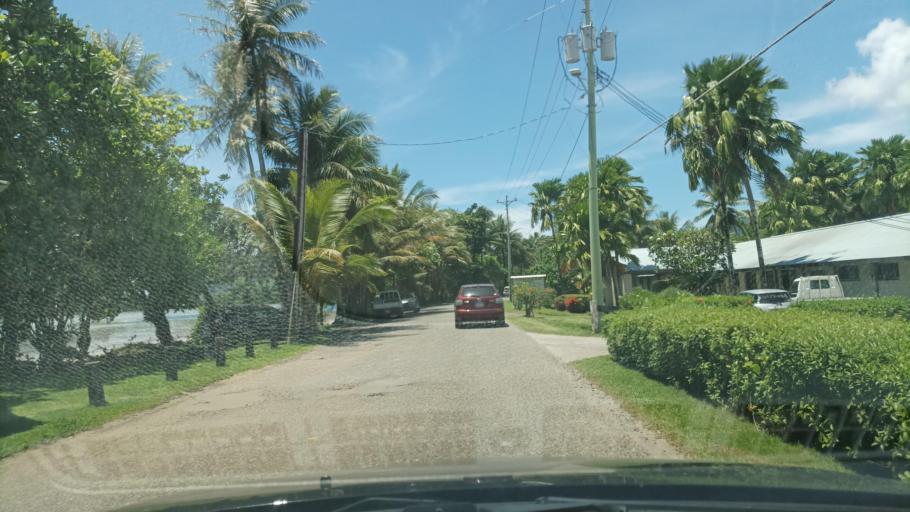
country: FM
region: Kosrae
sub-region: Lelu Municipality
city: Lelu
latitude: 5.3423
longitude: 163.0197
